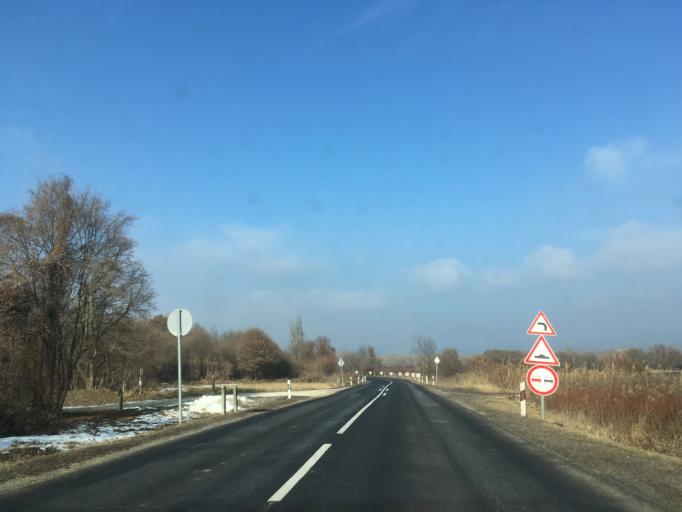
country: HU
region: Komarom-Esztergom
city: Pilismarot
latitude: 47.7944
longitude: 18.8647
